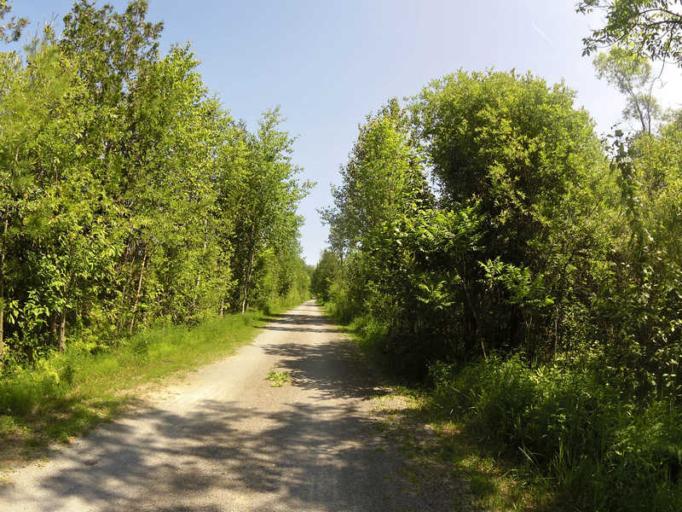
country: CA
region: Ontario
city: Peterborough
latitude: 44.3883
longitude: -78.2677
